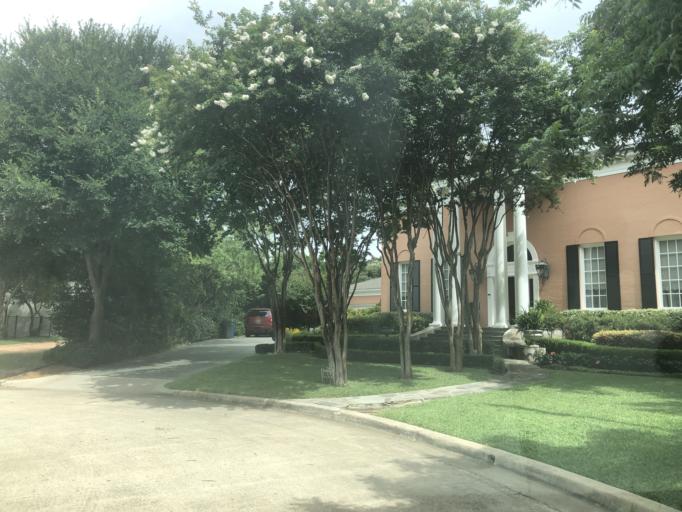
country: US
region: Texas
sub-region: Dallas County
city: University Park
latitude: 32.8657
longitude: -96.8349
